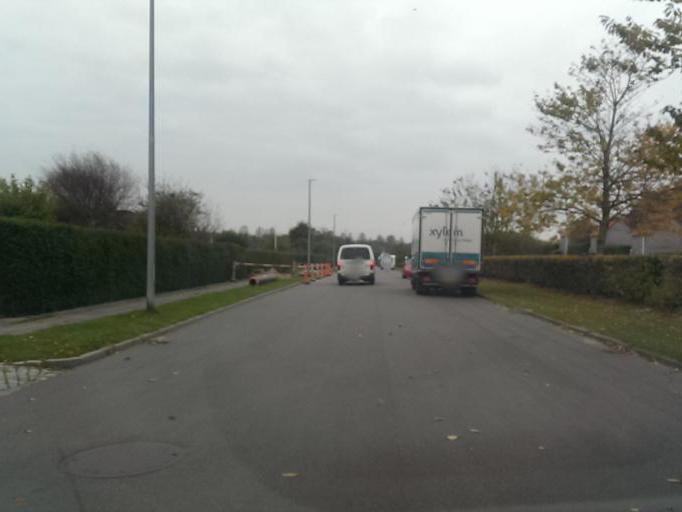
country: DK
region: South Denmark
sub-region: Esbjerg Kommune
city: Esbjerg
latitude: 55.5228
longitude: 8.4446
